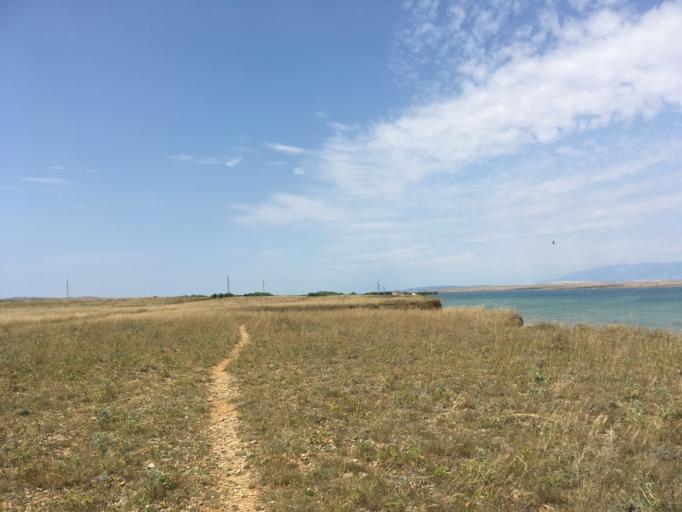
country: HR
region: Zadarska
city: Privlaka
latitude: 44.2719
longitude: 15.1499
